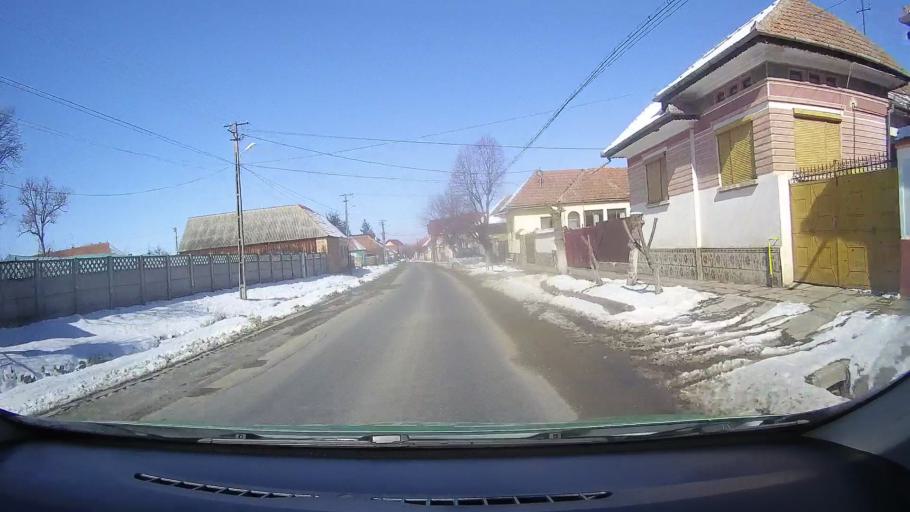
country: RO
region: Brasov
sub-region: Comuna Harseni
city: Harseni
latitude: 45.7514
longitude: 25.0138
